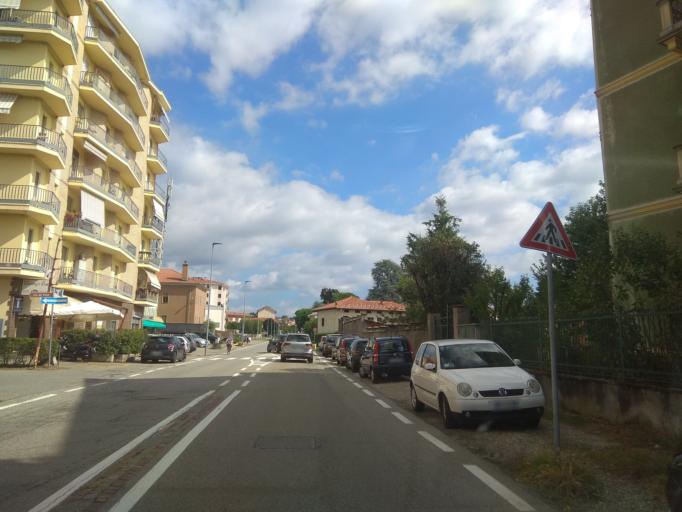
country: IT
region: Piedmont
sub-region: Provincia di Biella
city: Cossato
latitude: 45.5721
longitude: 8.1777
